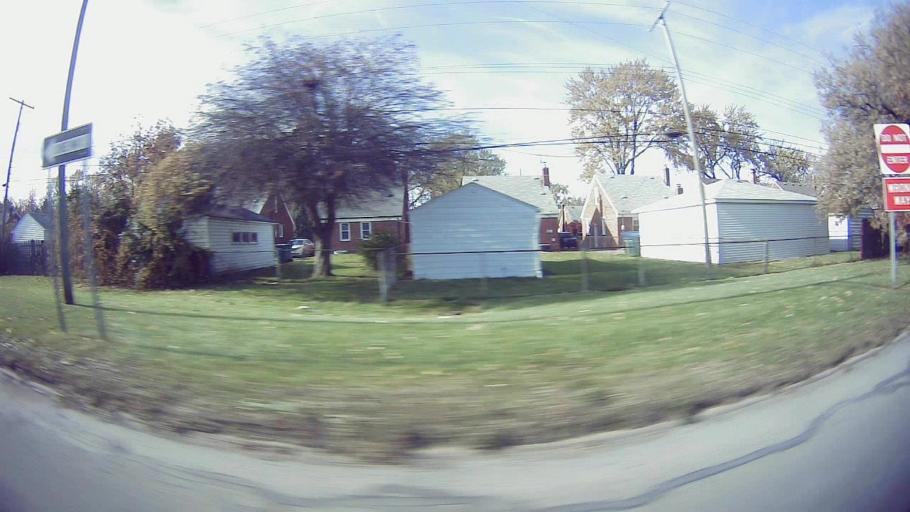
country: US
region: Michigan
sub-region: Wayne County
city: Dearborn Heights
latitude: 42.3243
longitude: -83.2728
